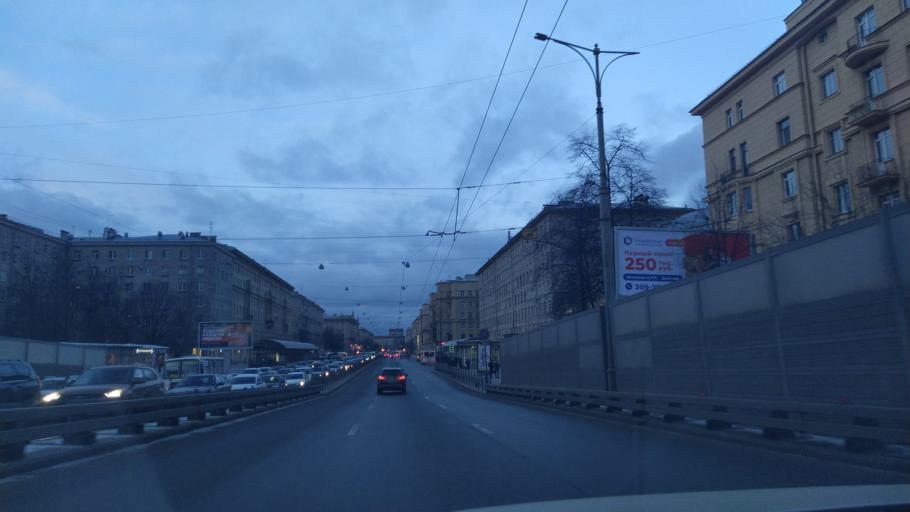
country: RU
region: St.-Petersburg
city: Avtovo
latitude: 59.8666
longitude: 30.2609
